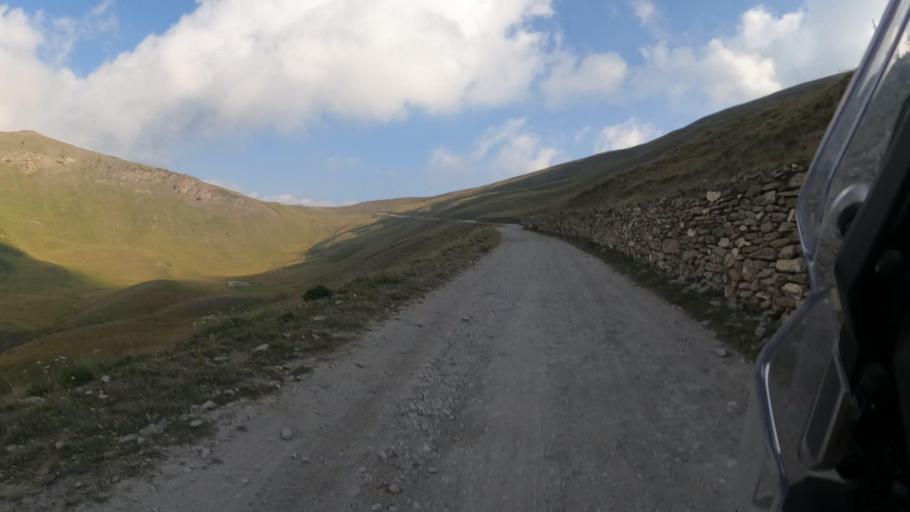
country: IT
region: Piedmont
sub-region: Provincia di Torino
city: Exilles
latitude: 45.0666
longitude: 6.9631
